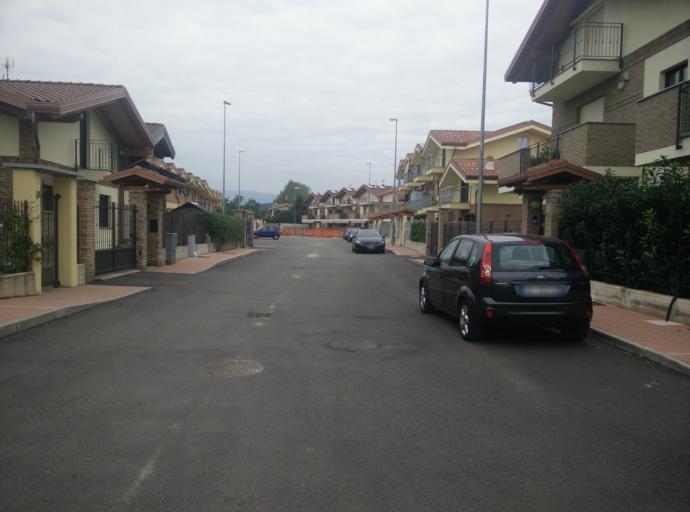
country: IT
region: Piedmont
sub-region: Provincia di Torino
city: Rivalta di Torino
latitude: 45.0225
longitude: 7.5212
